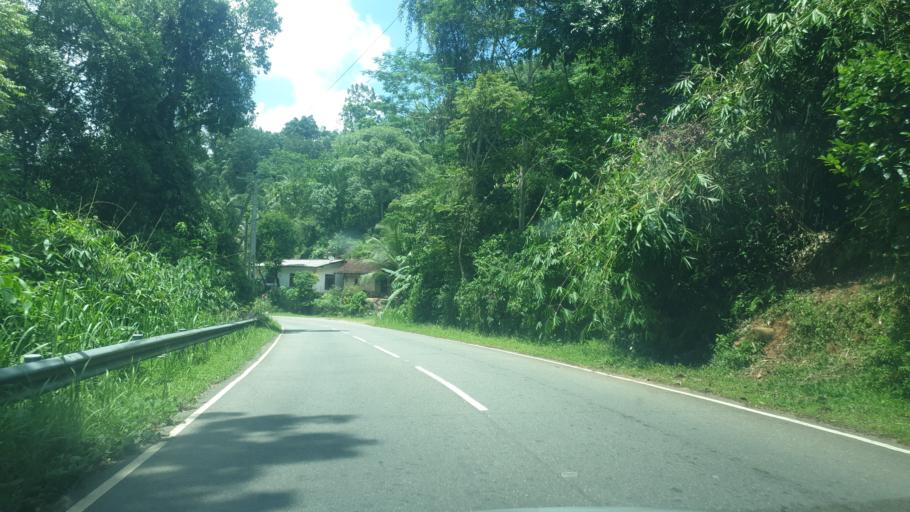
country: LK
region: Western
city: Horawala Junction
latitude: 6.5428
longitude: 80.2778
